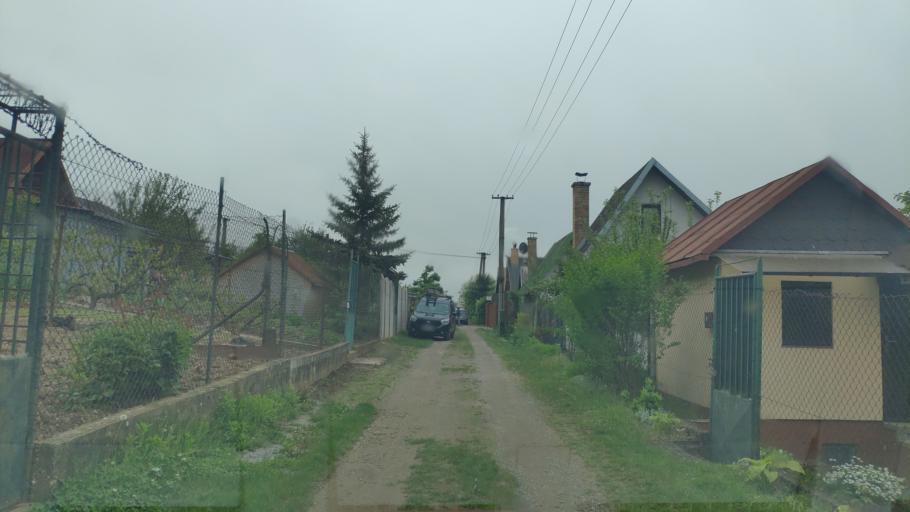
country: SK
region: Kosicky
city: Kosice
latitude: 48.6335
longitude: 21.1797
